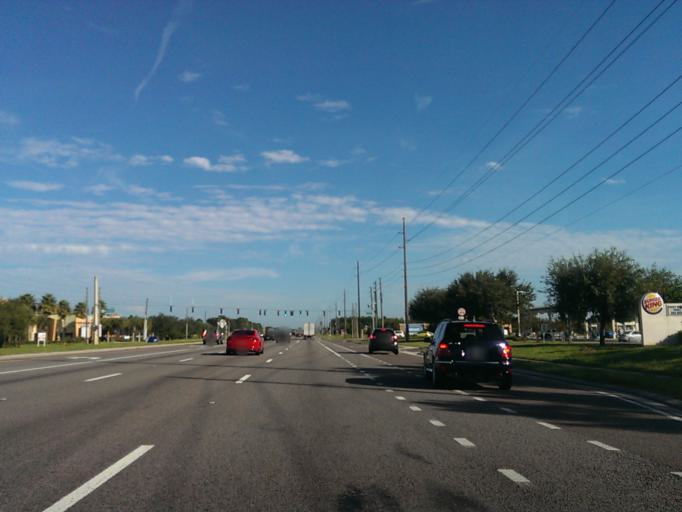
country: US
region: Florida
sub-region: Lake County
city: Four Corners
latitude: 28.3537
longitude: -81.6763
